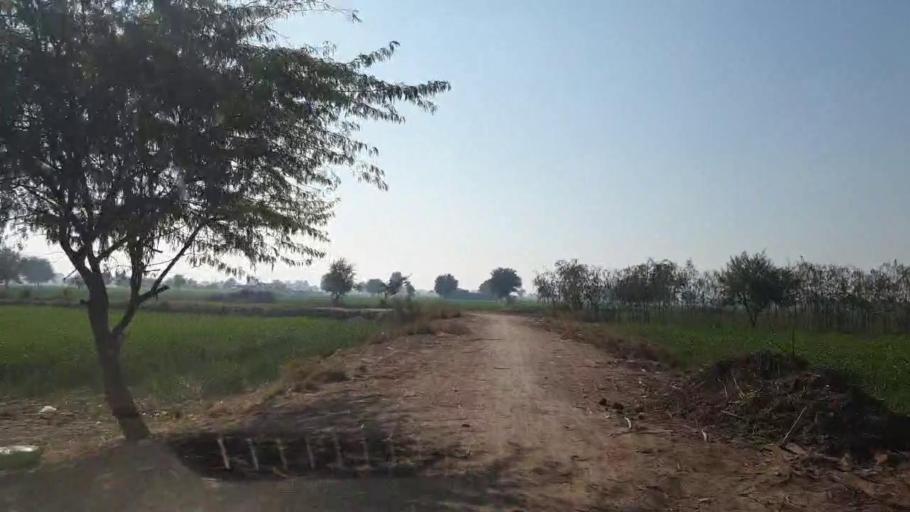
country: PK
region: Sindh
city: Nawabshah
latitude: 26.0813
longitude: 68.4789
